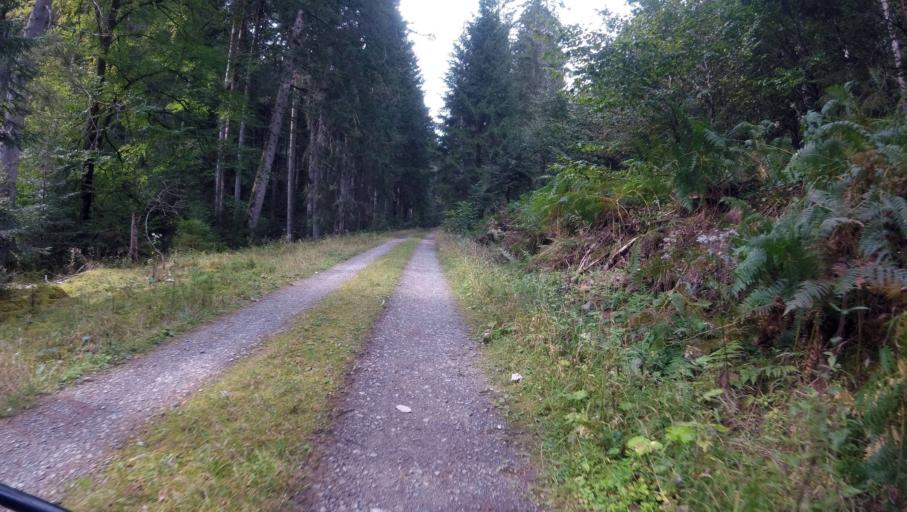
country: DE
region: Baden-Wuerttemberg
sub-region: Karlsruhe Region
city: Simmersfeld
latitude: 48.5930
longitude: 8.5066
